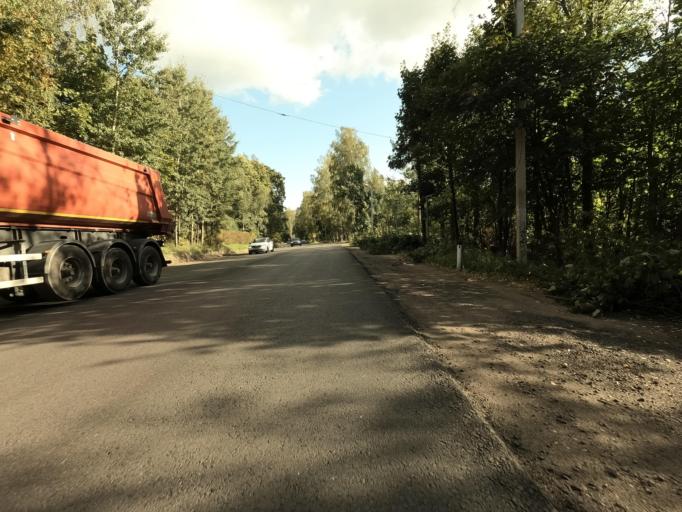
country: RU
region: Leningrad
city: Koltushi
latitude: 59.9404
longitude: 30.6572
